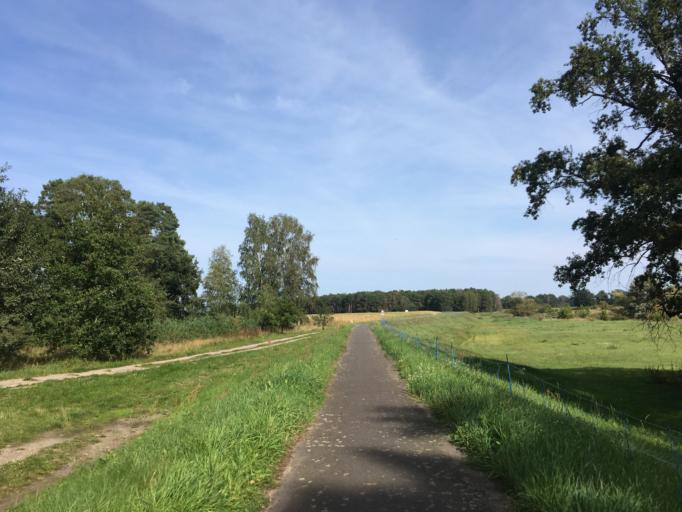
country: PL
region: Lubusz
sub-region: Powiat krosnienski
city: Gubin
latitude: 52.0187
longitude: 14.7317
